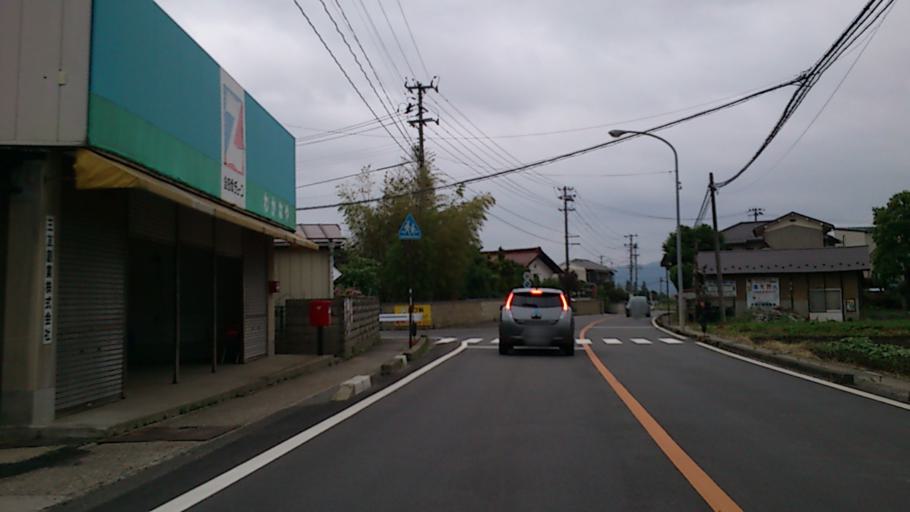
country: JP
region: Fukushima
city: Fukushima-shi
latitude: 37.7586
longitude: 140.4112
